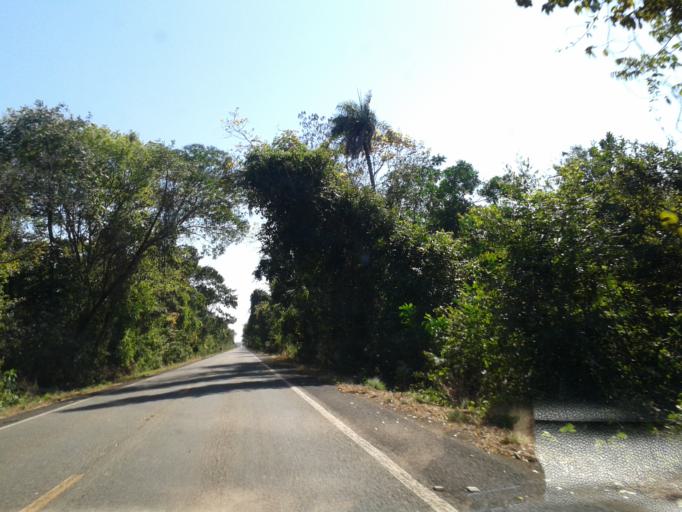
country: BR
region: Goias
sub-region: Crixas
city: Crixas
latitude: -14.0134
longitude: -50.3260
